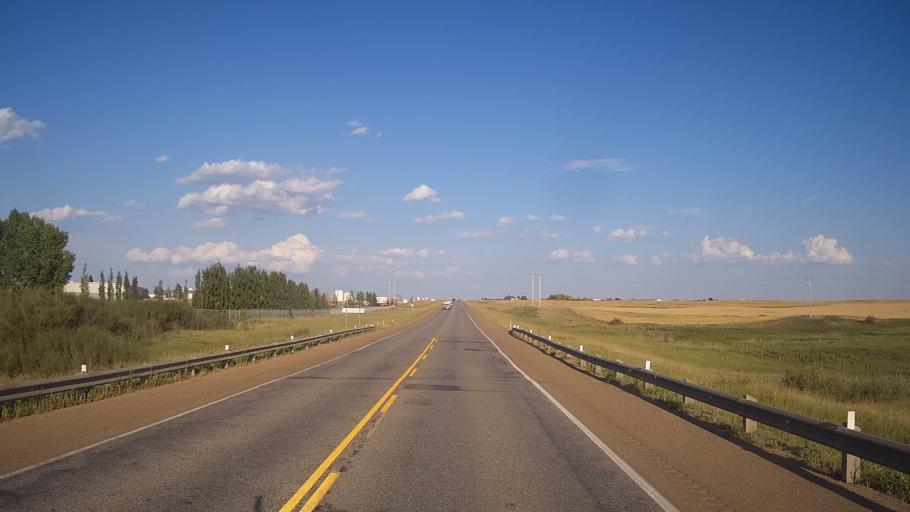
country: CA
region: Alberta
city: Hanna
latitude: 51.6333
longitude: -111.9357
